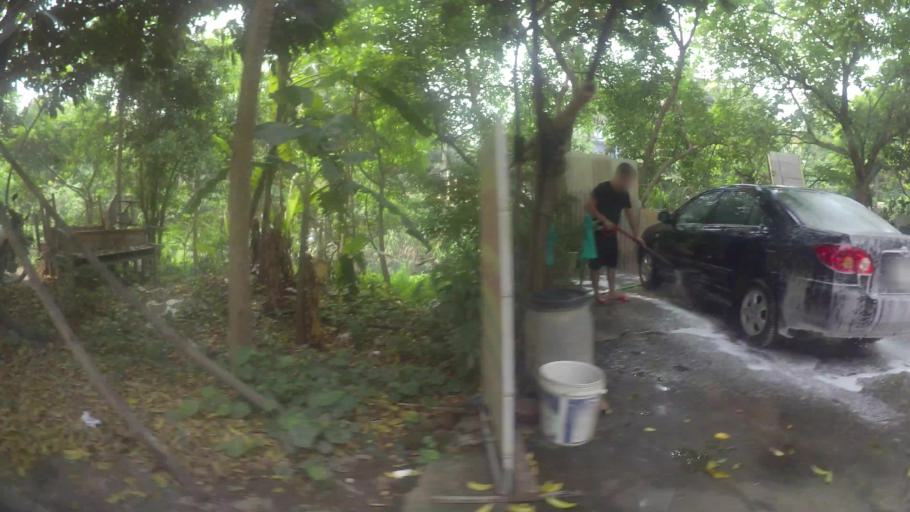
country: VN
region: Ha Noi
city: Ha Dong
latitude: 20.9708
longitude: 105.7584
